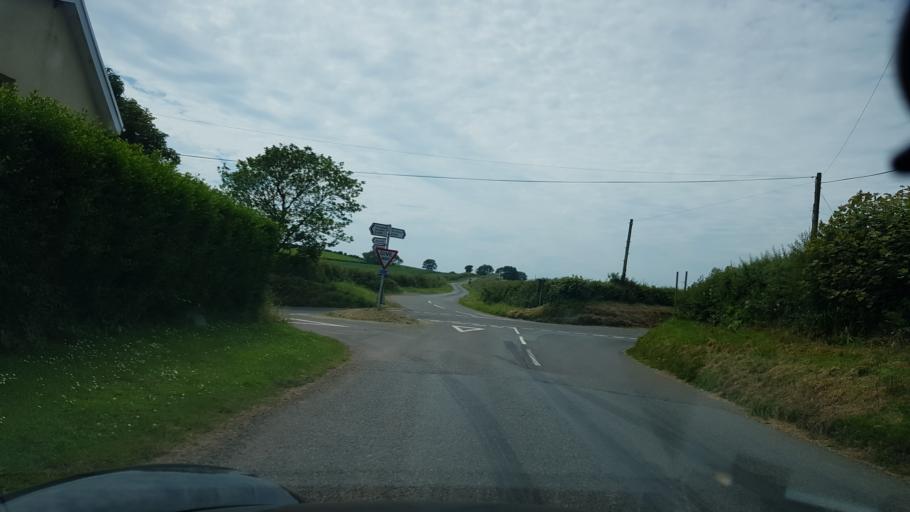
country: GB
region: Wales
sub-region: Carmarthenshire
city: Llanddowror
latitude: 51.7633
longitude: -4.5540
